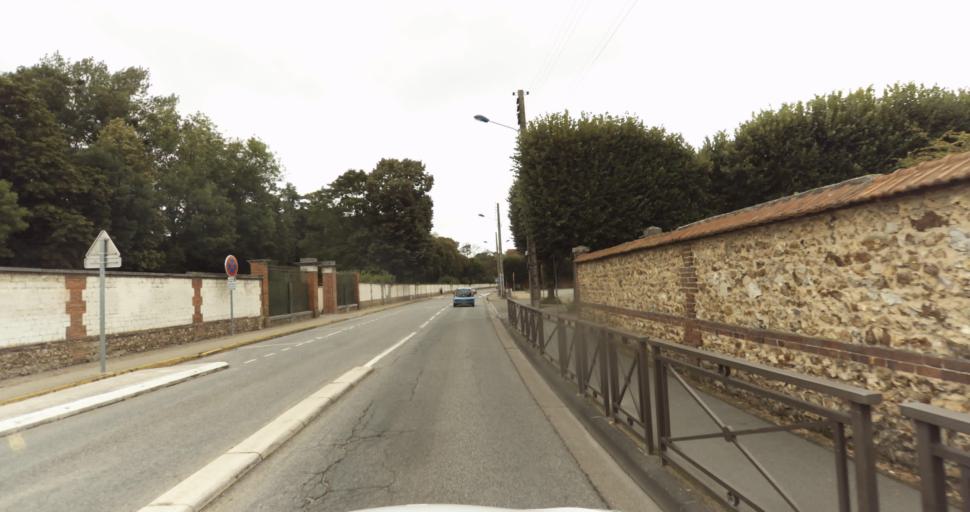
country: FR
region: Haute-Normandie
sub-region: Departement de l'Eure
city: Evreux
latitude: 49.0180
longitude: 1.1250
